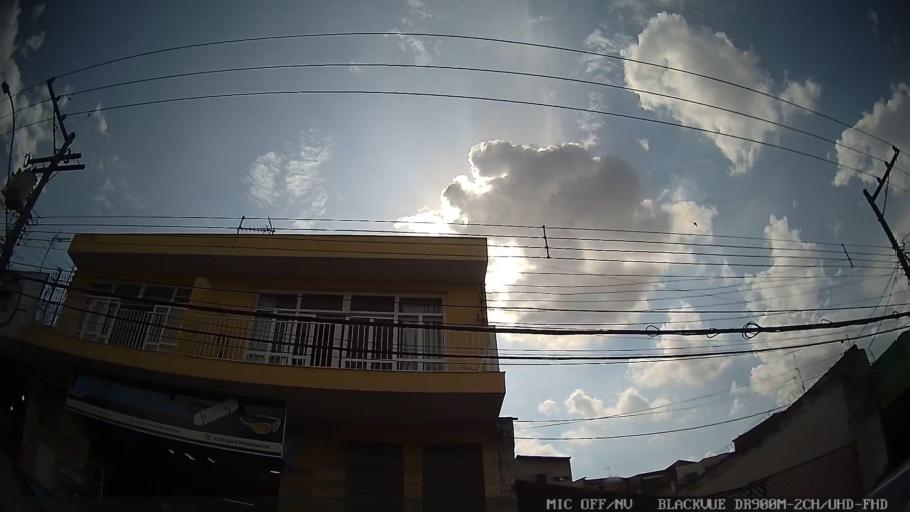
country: BR
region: Sao Paulo
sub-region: Braganca Paulista
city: Braganca Paulista
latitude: -22.9515
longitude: -46.5404
